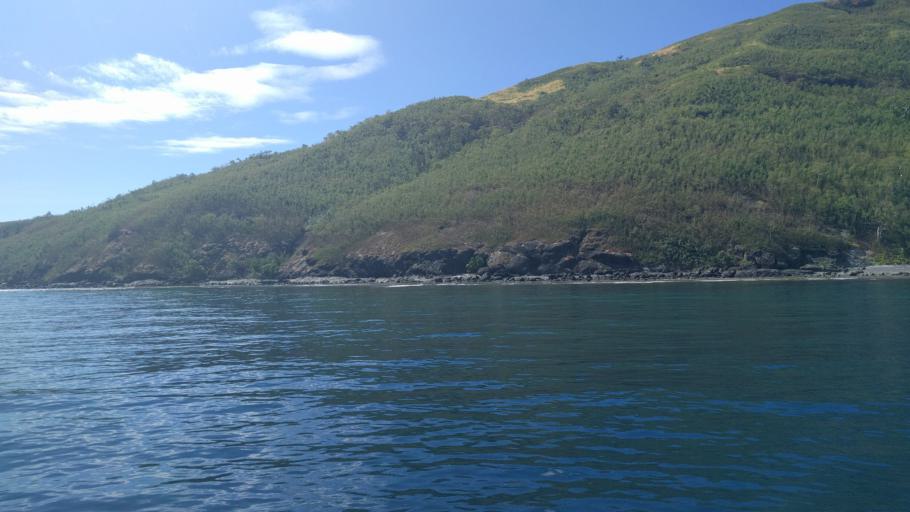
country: FJ
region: Western
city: Lautoka
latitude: -17.2830
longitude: 177.1031
